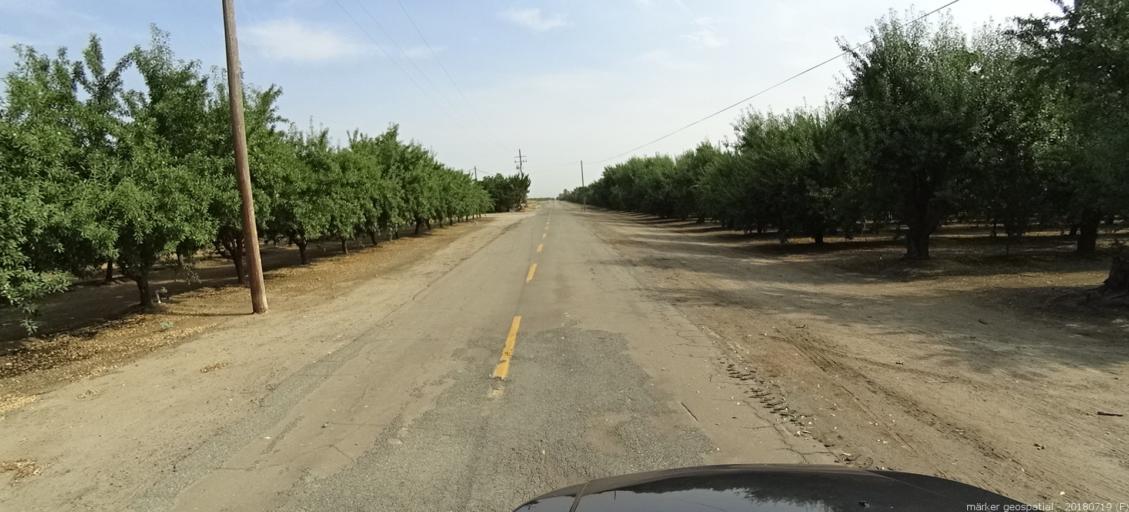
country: US
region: California
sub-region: Madera County
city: Fairmead
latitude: 37.0789
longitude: -120.1750
